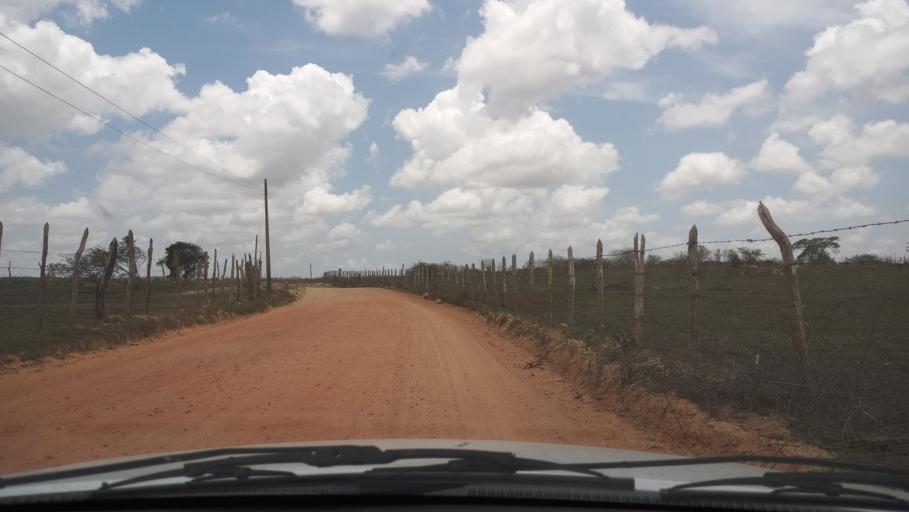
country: BR
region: Rio Grande do Norte
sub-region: Brejinho
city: Brejinho
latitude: -6.2820
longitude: -35.3390
